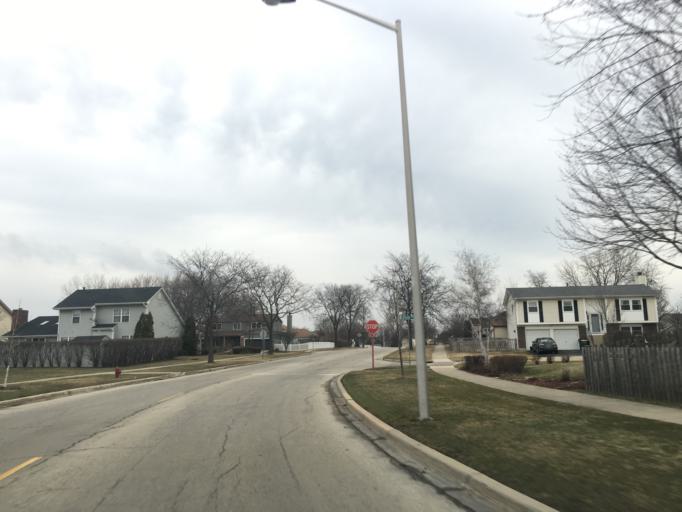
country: US
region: Illinois
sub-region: Cook County
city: Schaumburg
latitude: 42.0434
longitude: -88.1086
